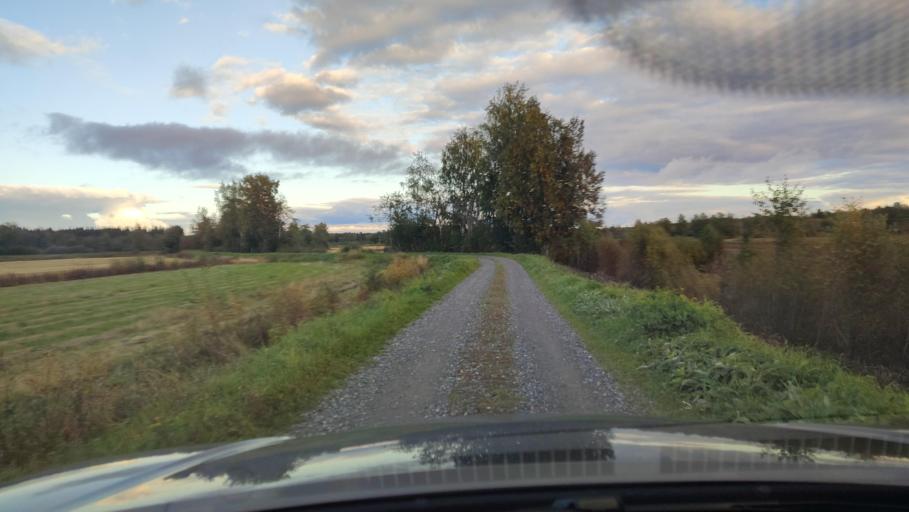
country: FI
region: Ostrobothnia
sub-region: Sydosterbotten
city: Kristinestad
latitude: 62.2383
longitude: 21.4507
